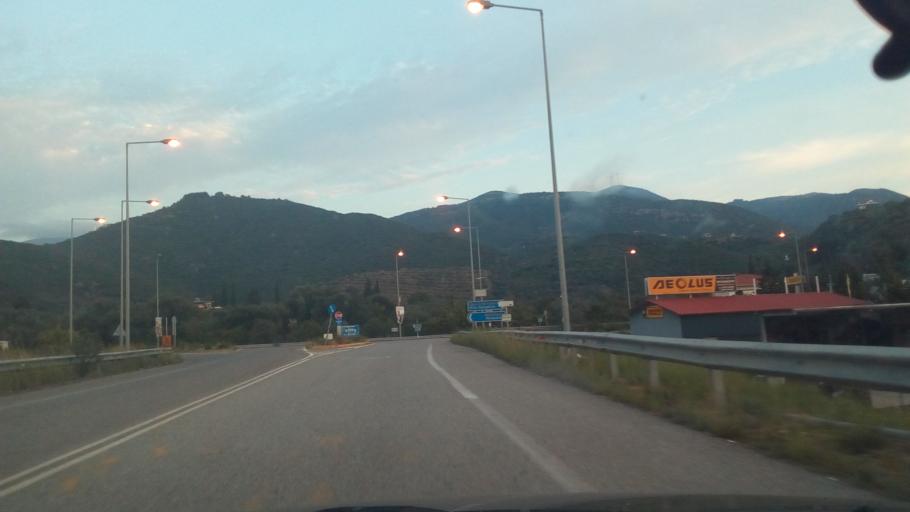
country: GR
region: West Greece
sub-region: Nomos Aitolias kai Akarnanias
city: Nafpaktos
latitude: 38.4084
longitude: 21.8684
